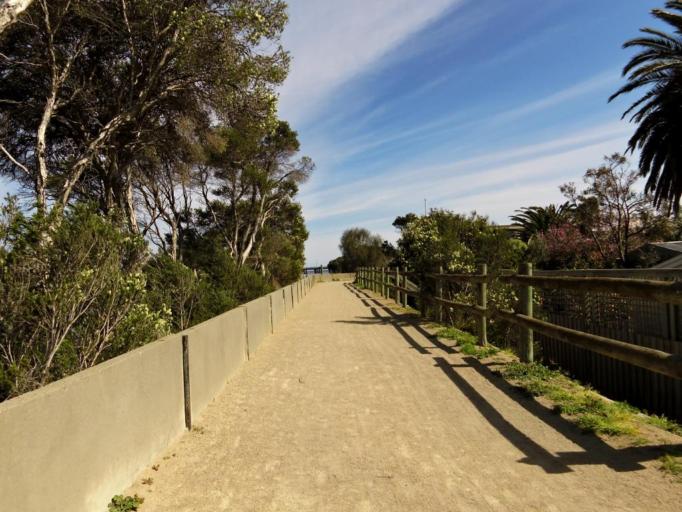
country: AU
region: Victoria
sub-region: Kingston
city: Bonbeach
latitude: -38.0696
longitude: 145.1289
